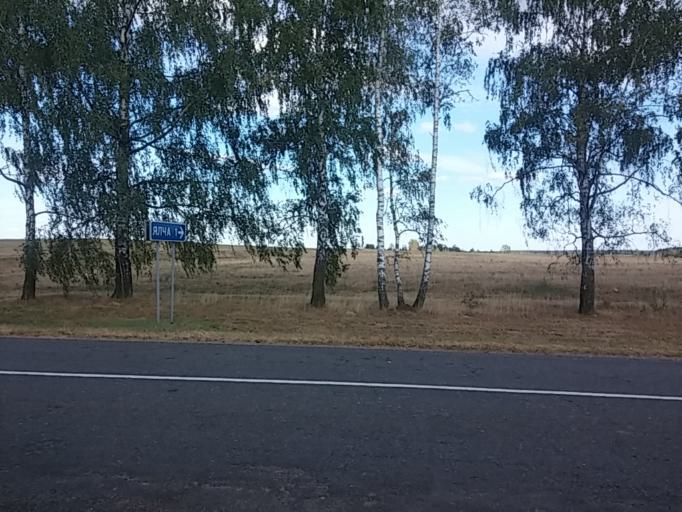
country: BY
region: Minsk
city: Chervyen'
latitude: 53.7779
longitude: 28.2415
